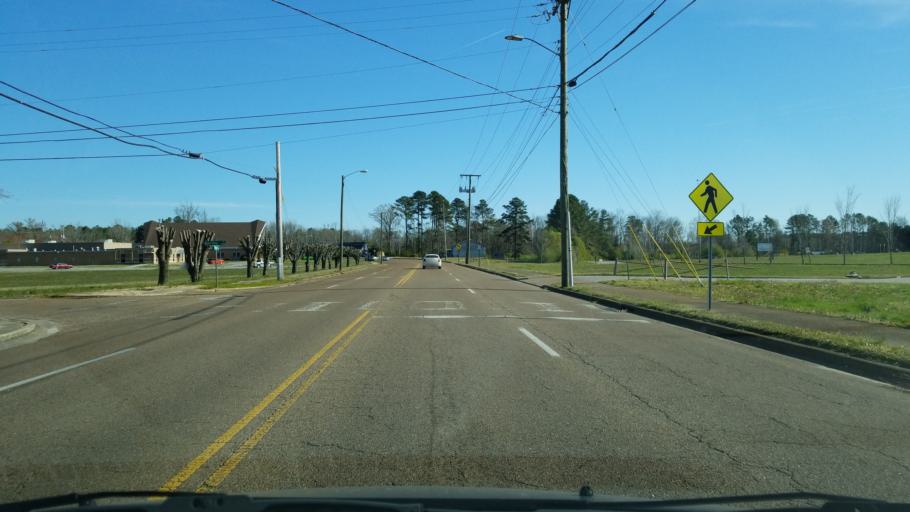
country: US
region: Tennessee
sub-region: Hamilton County
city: East Ridge
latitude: 35.0285
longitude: -85.2197
